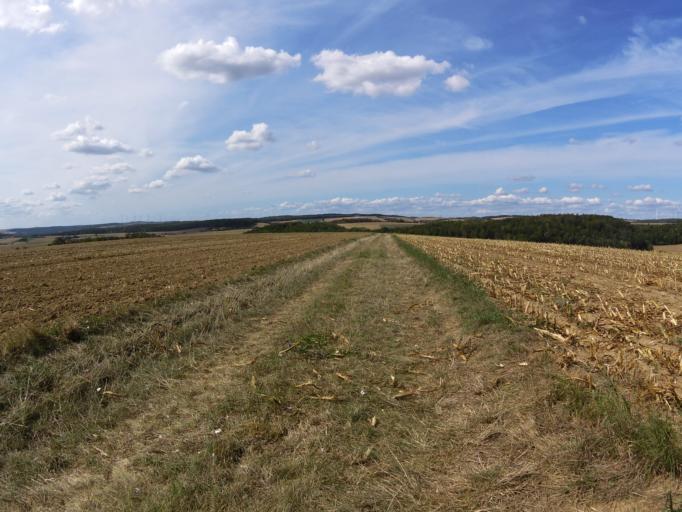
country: DE
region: Bavaria
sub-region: Regierungsbezirk Unterfranken
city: Rimpar
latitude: 49.8629
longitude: 9.9338
